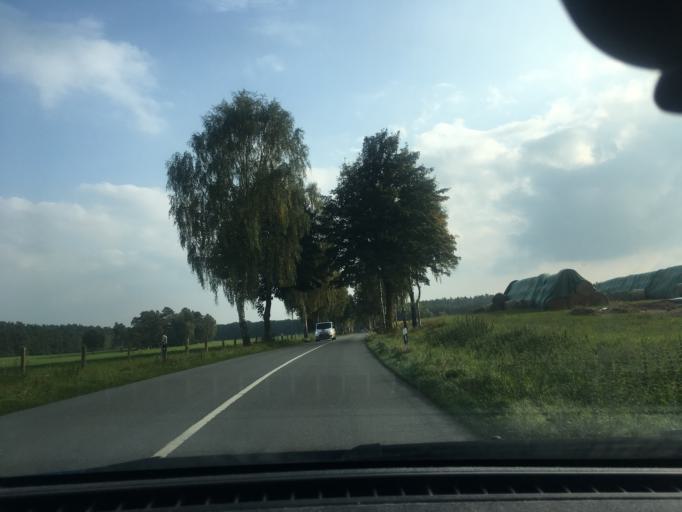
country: DE
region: Lower Saxony
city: Rullstorf
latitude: 53.2669
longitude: 10.5189
